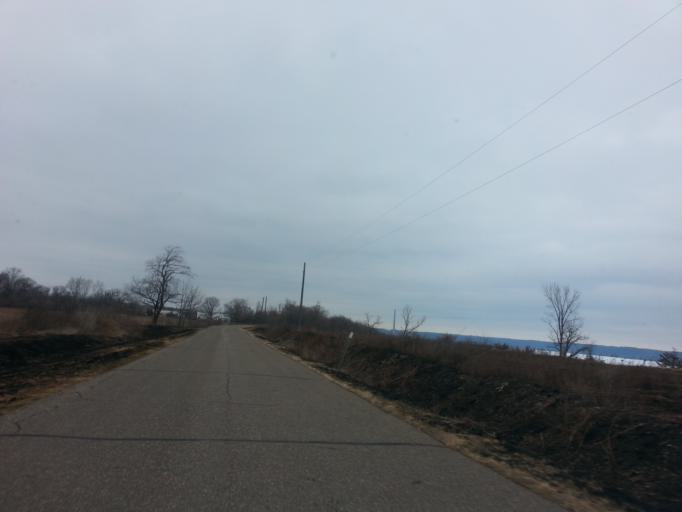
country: US
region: Wisconsin
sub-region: Saint Croix County
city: North Hudson
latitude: 44.9862
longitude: -92.7772
